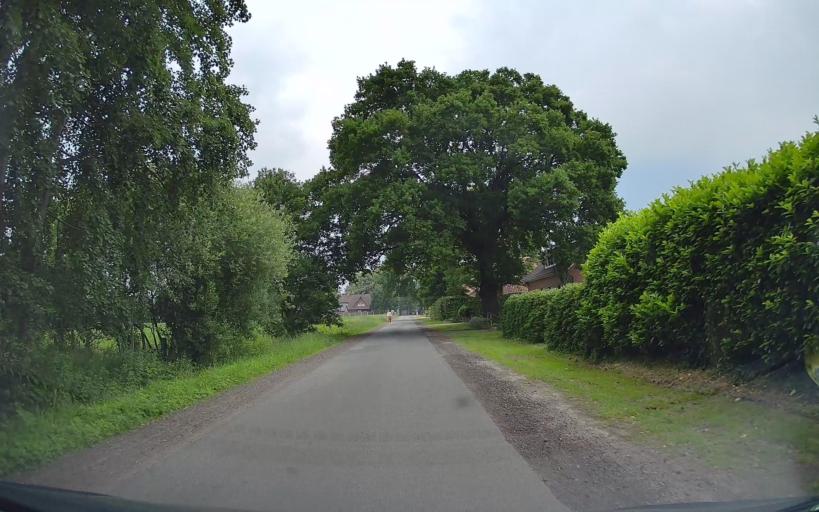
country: DE
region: Lower Saxony
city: Friesoythe
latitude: 53.0401
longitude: 7.8460
